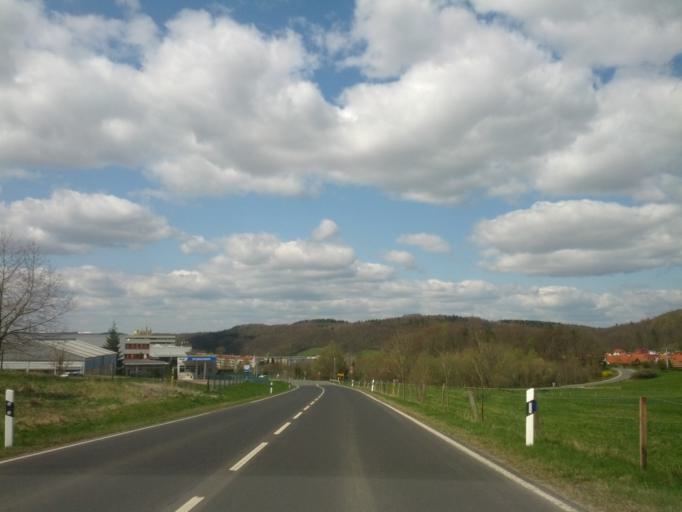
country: DE
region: Thuringia
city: Seebach
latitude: 50.9055
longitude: 10.4353
